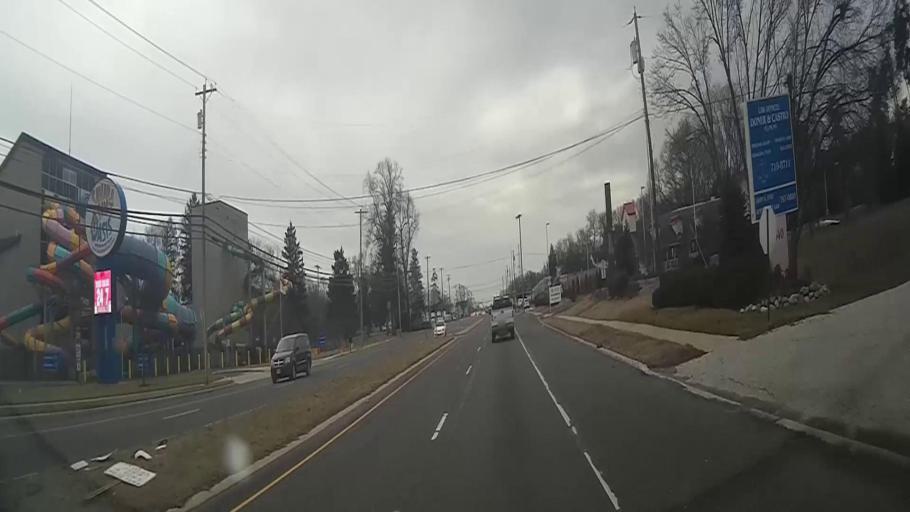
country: US
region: New Jersey
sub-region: Camden County
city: Berlin
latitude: 39.8165
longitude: -74.9298
